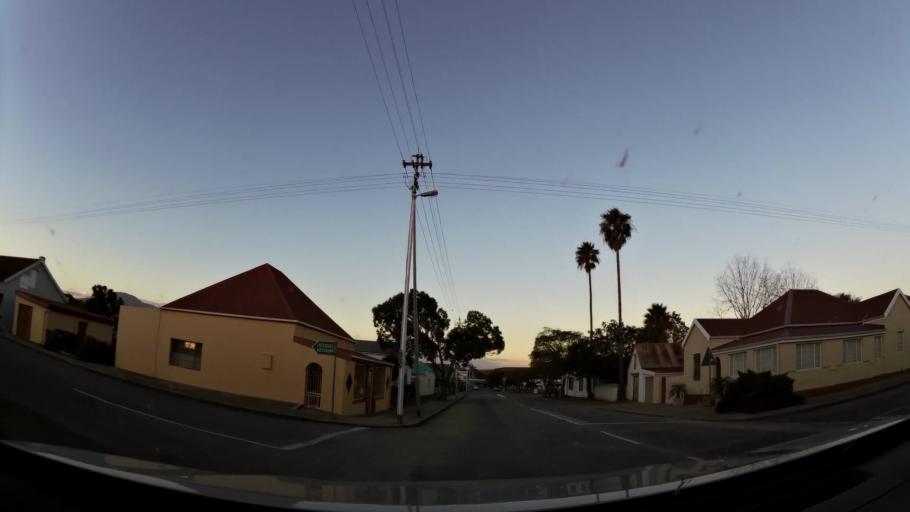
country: ZA
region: Western Cape
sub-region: Eden District Municipality
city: Riversdale
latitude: -34.0911
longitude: 21.2575
